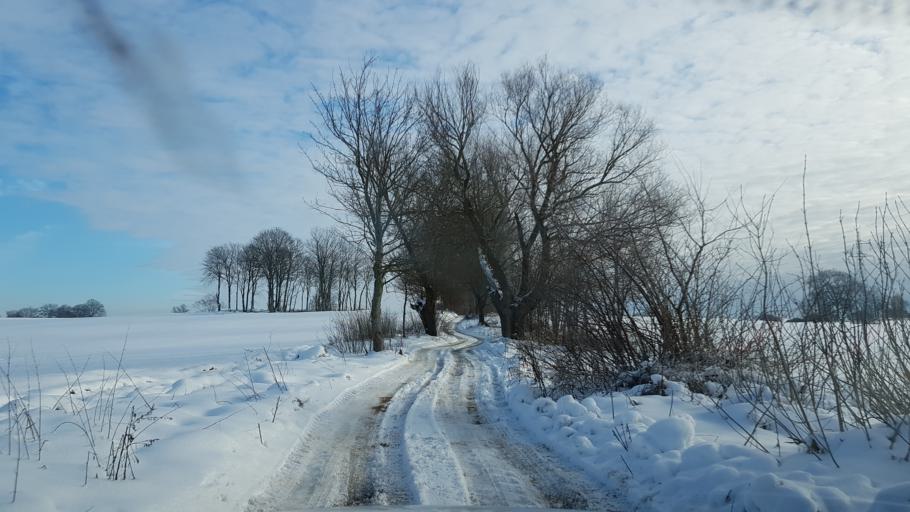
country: PL
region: West Pomeranian Voivodeship
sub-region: Powiat drawski
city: Drawsko Pomorskie
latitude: 53.5335
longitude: 15.7766
